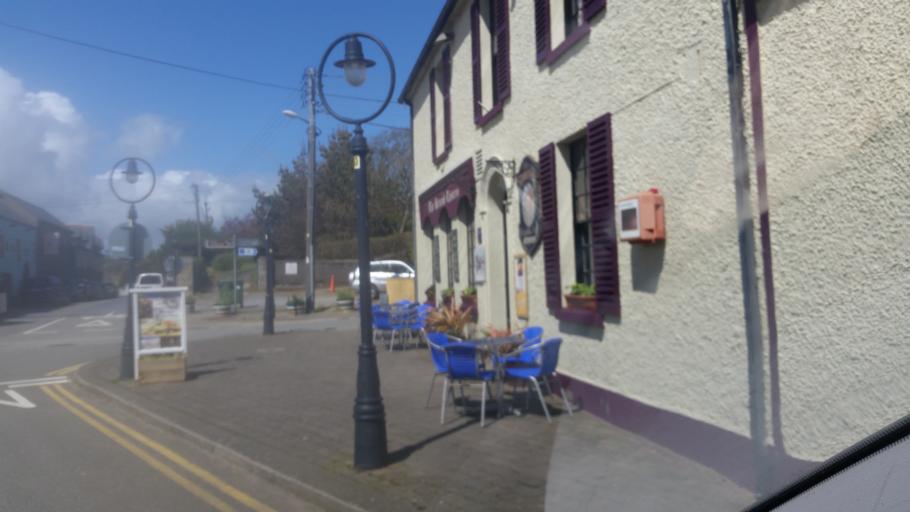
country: IE
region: Munster
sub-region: Waterford
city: Dunmore East
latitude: 52.2210
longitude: -6.9335
